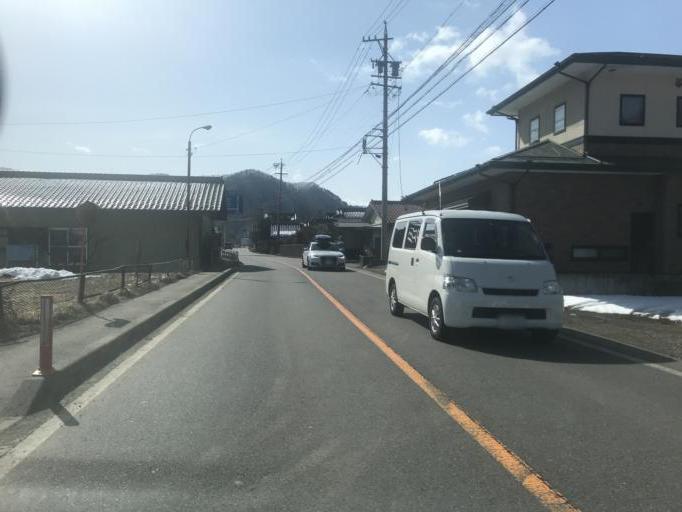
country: JP
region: Nagano
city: Saku
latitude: 36.0239
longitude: 138.4894
